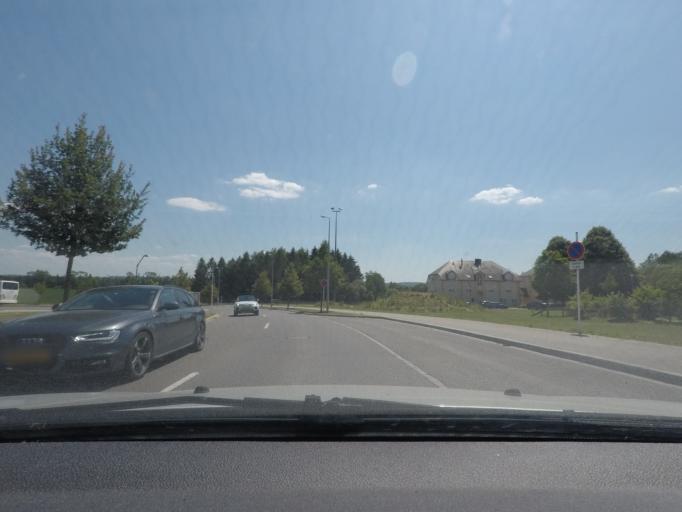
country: LU
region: Diekirch
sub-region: Canton de Redange
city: Redange-sur-Attert
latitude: 49.7692
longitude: 5.8978
